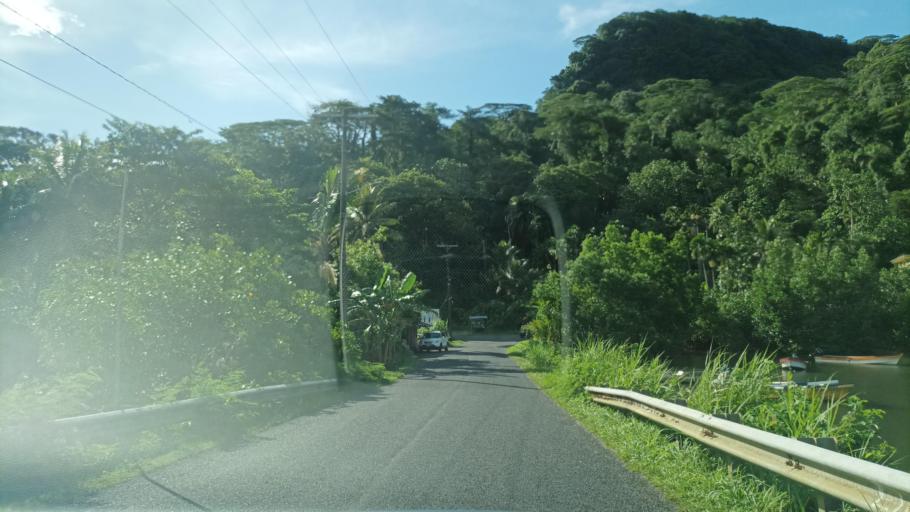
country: FM
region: Pohnpei
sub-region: Kolonia Municipality
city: Kolonia Town
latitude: 6.9573
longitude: 158.1954
